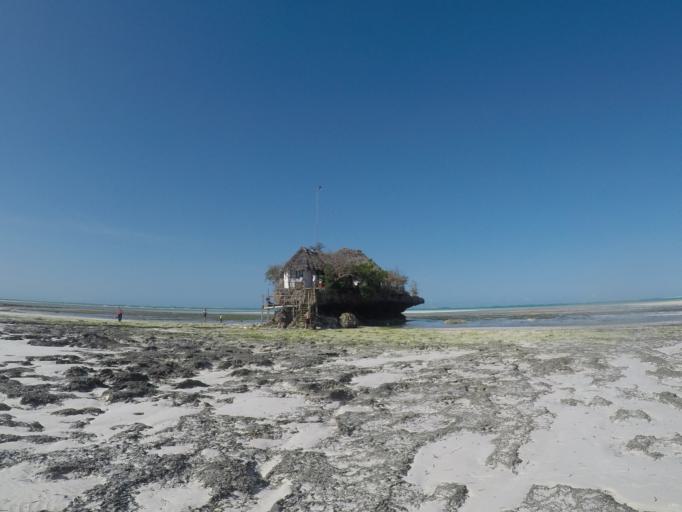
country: TZ
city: Kiwengwa
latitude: -6.1524
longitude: 39.5190
